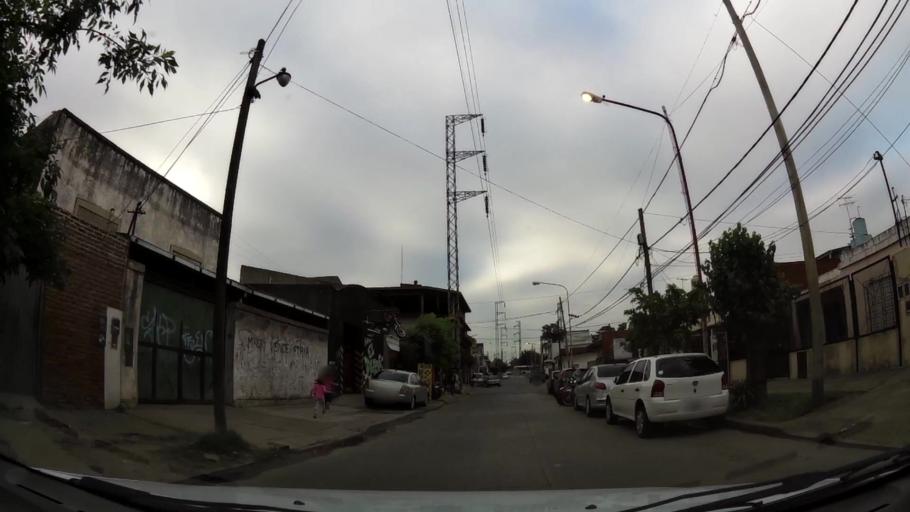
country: AR
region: Buenos Aires
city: San Justo
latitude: -34.7022
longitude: -58.5786
